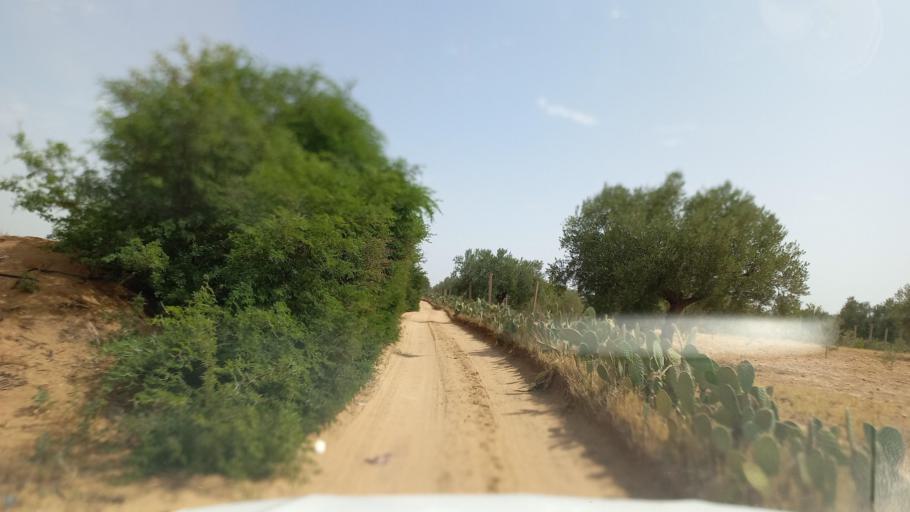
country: TN
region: Al Qasrayn
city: Kasserine
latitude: 35.2571
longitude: 9.0539
